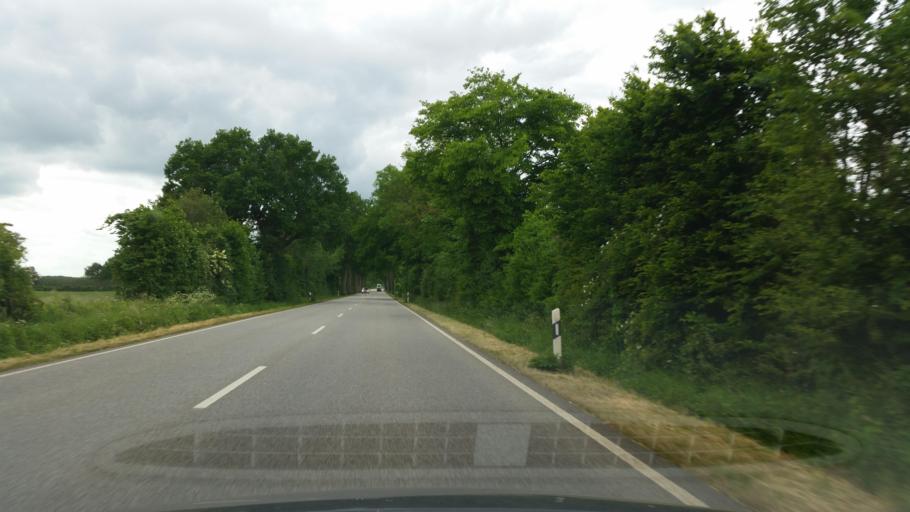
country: DE
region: Schleswig-Holstein
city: Travenhorst
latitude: 53.9941
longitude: 10.4670
